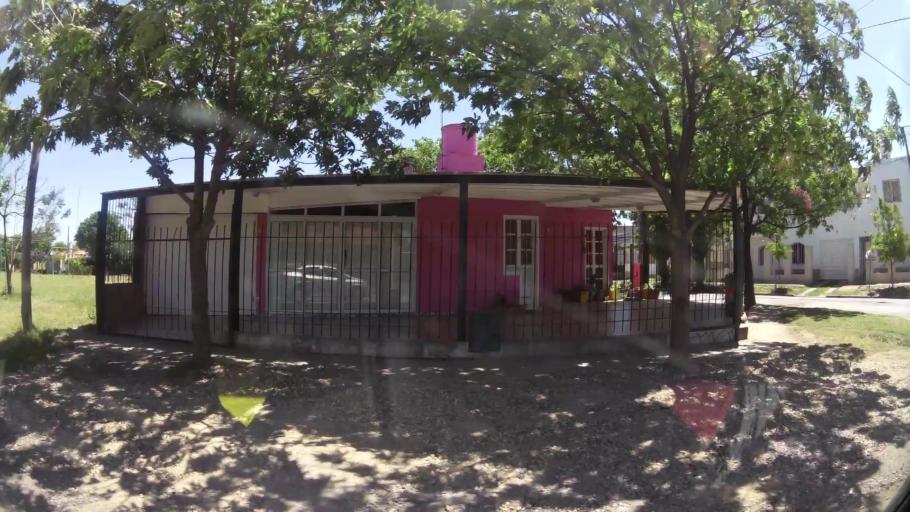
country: AR
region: Cordoba
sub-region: Departamento de Capital
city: Cordoba
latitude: -31.3853
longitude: -64.1413
